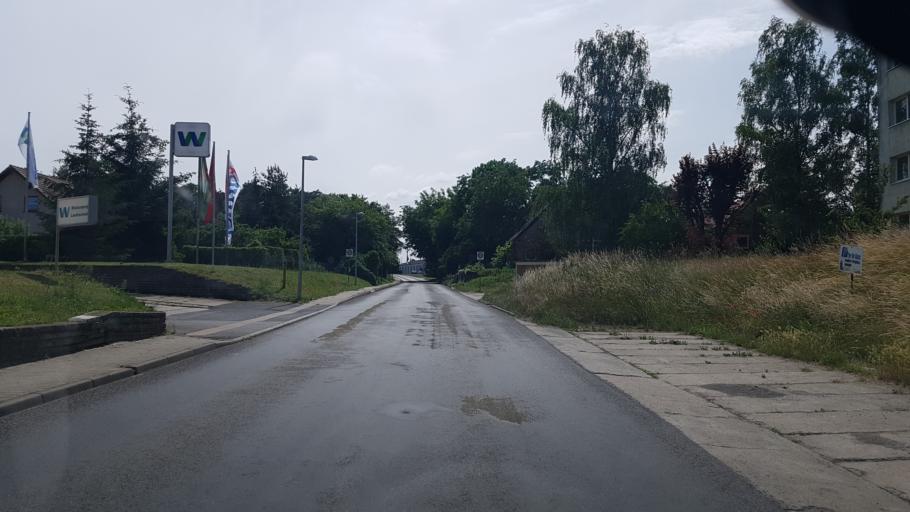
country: DE
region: Brandenburg
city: Prenzlau
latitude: 53.3600
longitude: 13.7971
